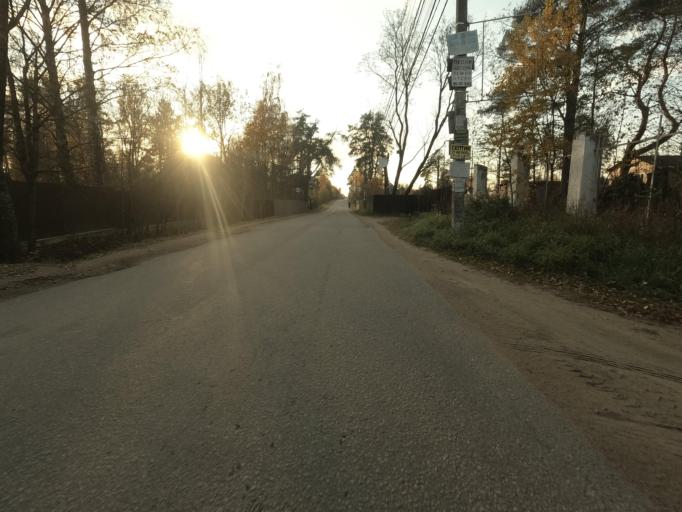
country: RU
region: St.-Petersburg
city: Beloostrov
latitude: 60.1889
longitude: 30.0875
